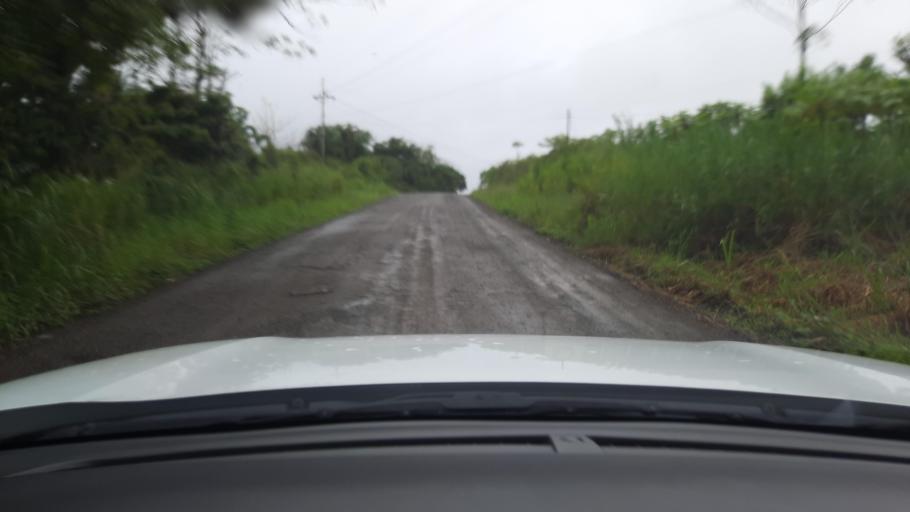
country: CR
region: Alajuela
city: San Jose
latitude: 11.0120
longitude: -85.3259
